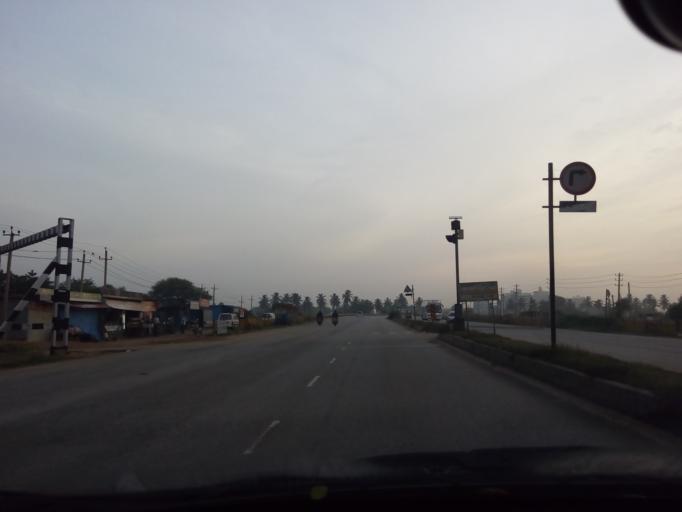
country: IN
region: Karnataka
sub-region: Bangalore Rural
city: Devanhalli
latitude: 13.2504
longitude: 77.7070
